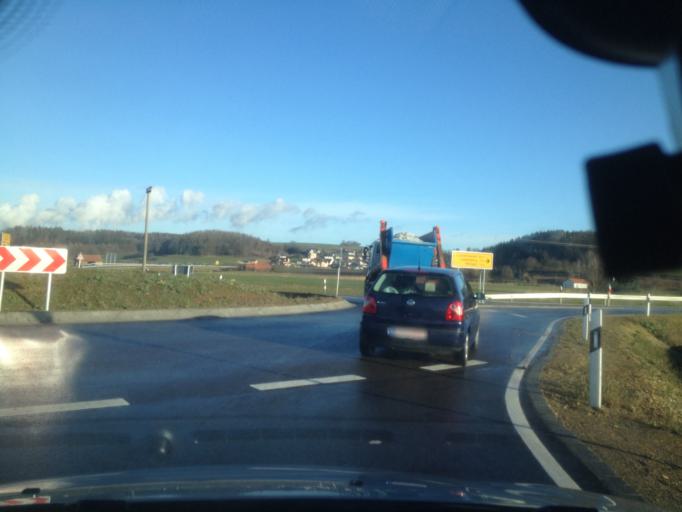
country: DE
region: Bavaria
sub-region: Swabia
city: Rofingen
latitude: 48.4271
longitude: 10.4353
